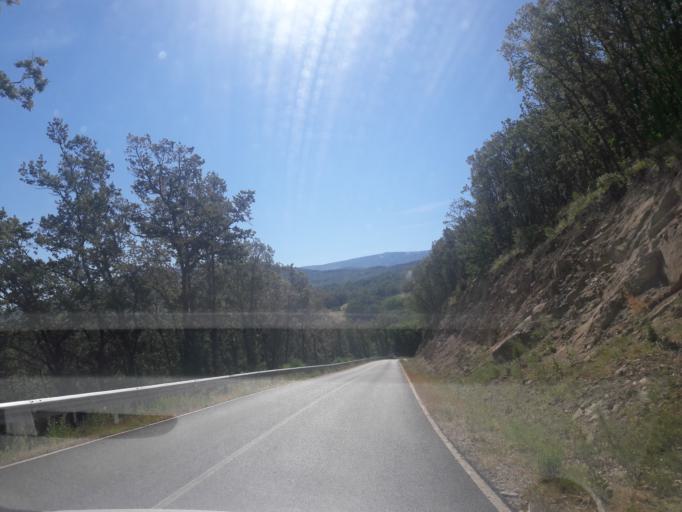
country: ES
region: Castille and Leon
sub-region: Provincia de Salamanca
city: Penacaballera
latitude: 40.3425
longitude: -5.8774
